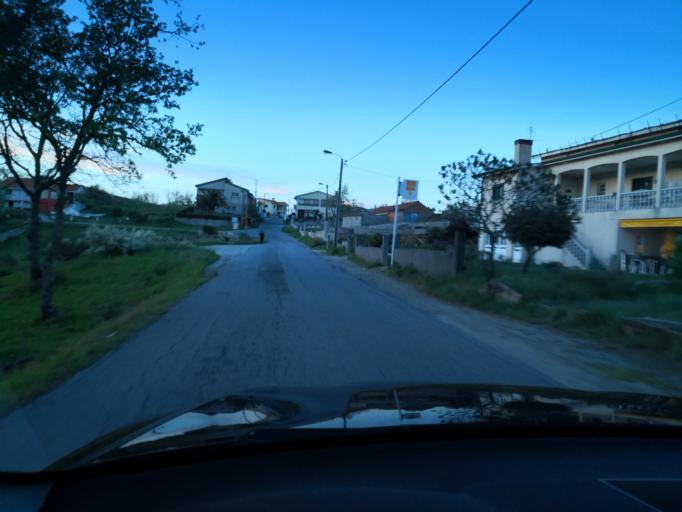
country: PT
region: Vila Real
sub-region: Vila Real
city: Vila Real
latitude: 41.3545
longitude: -7.6630
